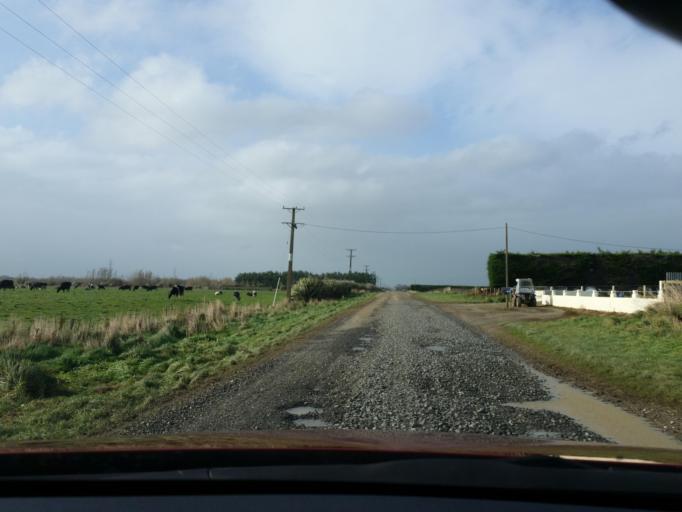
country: NZ
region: Southland
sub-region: Invercargill City
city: Invercargill
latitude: -46.3075
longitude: 168.3847
